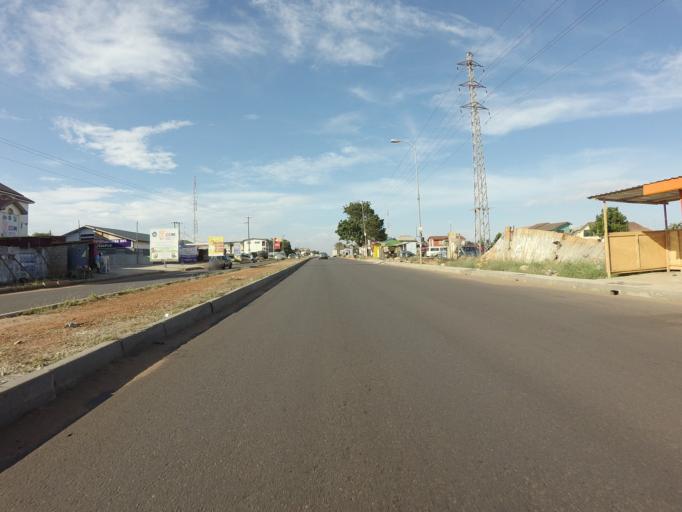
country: GH
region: Greater Accra
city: Nungua
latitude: 5.6256
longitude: -0.0684
